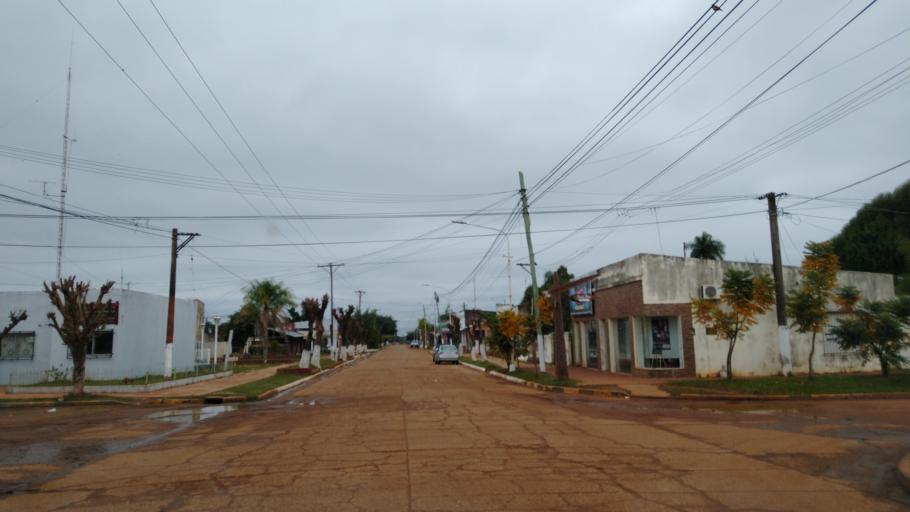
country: AR
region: Corrientes
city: Alvear
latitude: -29.0924
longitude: -56.5474
